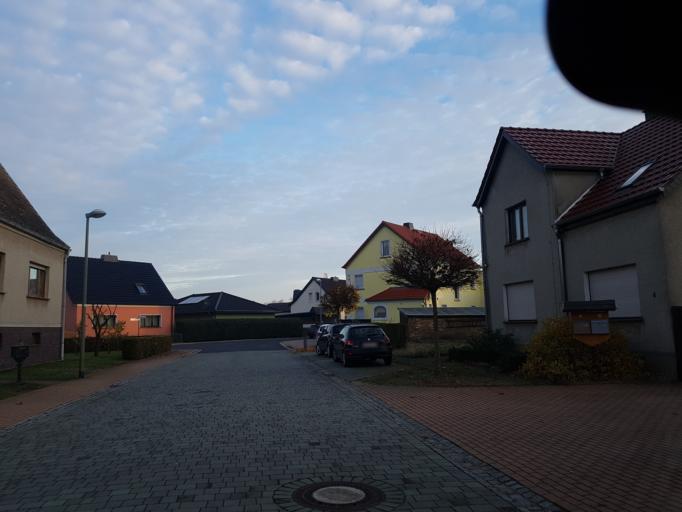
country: DE
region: Saxony-Anhalt
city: Elster
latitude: 51.8285
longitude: 12.8338
